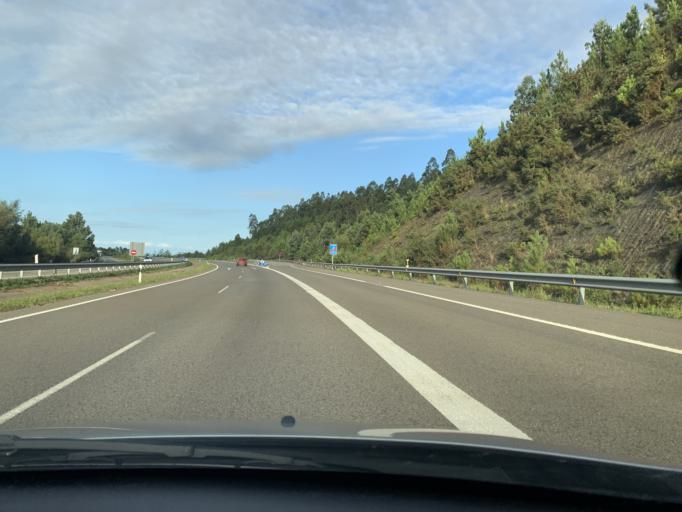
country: ES
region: Galicia
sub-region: Provincia de Lugo
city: Barreiros
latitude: 43.5352
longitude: -7.2309
